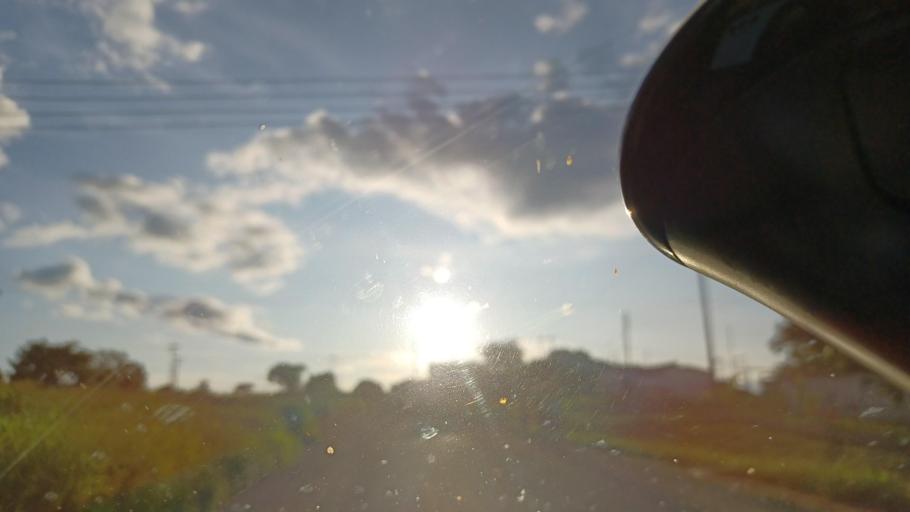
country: ZM
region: North-Western
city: Kasempa
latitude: -13.4581
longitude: 25.8438
